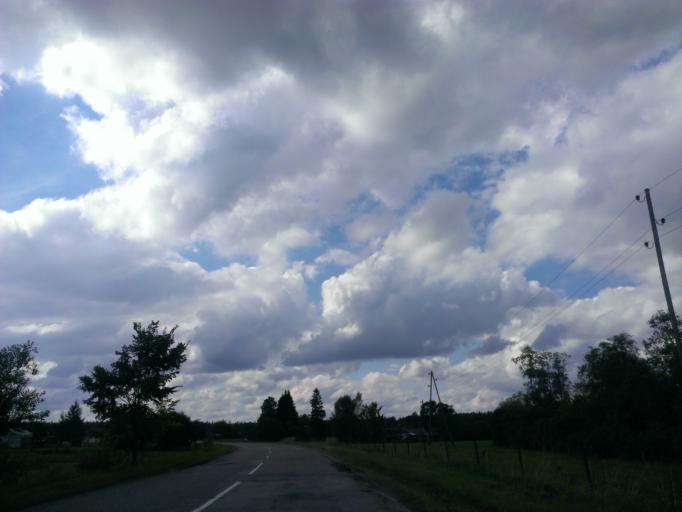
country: LV
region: Garkalne
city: Garkalne
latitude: 56.9656
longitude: 24.5123
